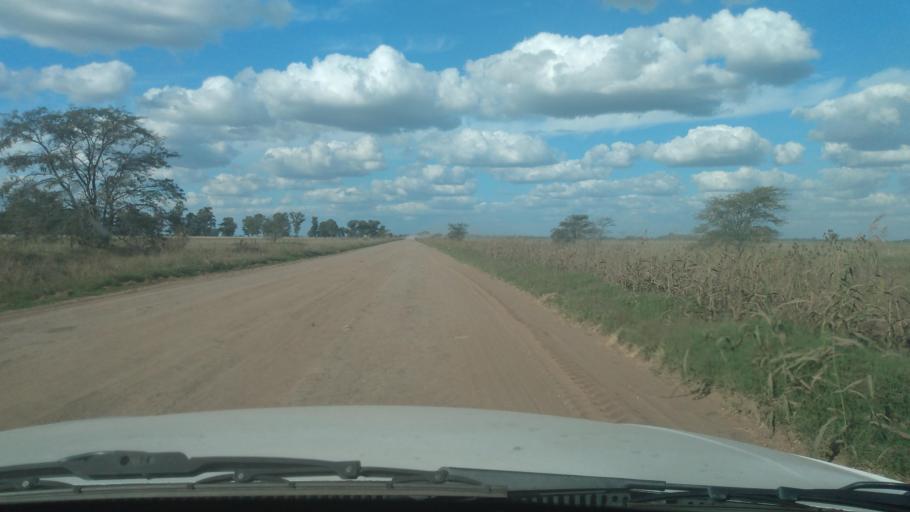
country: AR
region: Buenos Aires
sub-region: Partido de Navarro
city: Navarro
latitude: -35.0124
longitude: -59.4479
